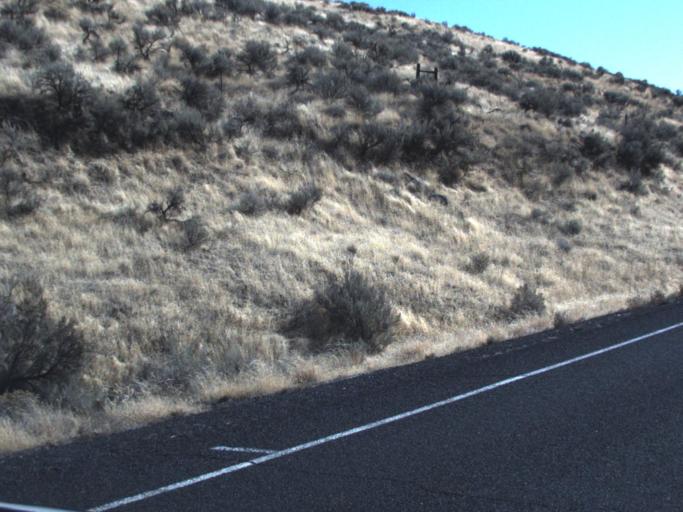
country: US
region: Washington
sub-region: Franklin County
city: Connell
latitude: 46.6644
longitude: -118.5478
